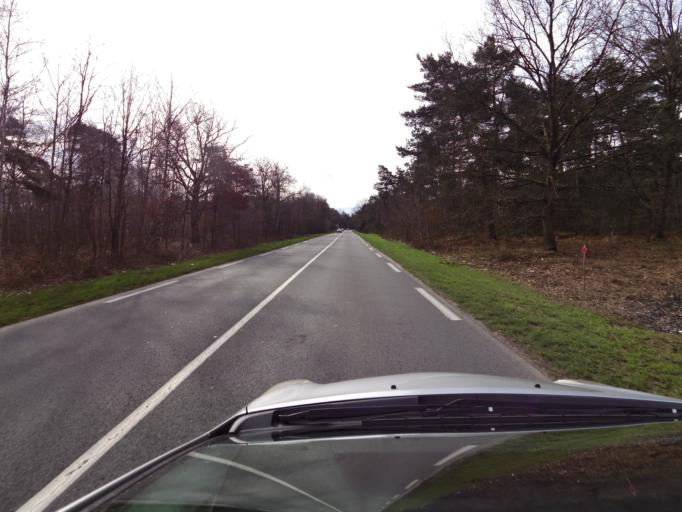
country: FR
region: Picardie
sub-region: Departement de l'Oise
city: Ver-sur-Launette
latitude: 49.1409
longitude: 2.6845
